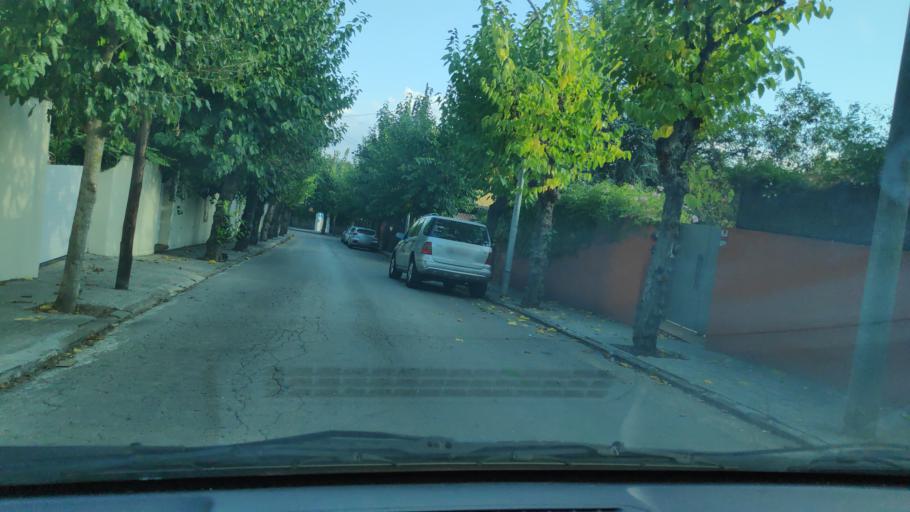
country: ES
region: Catalonia
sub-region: Provincia de Barcelona
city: Sant Quirze del Valles
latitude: 41.5019
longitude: 2.0867
